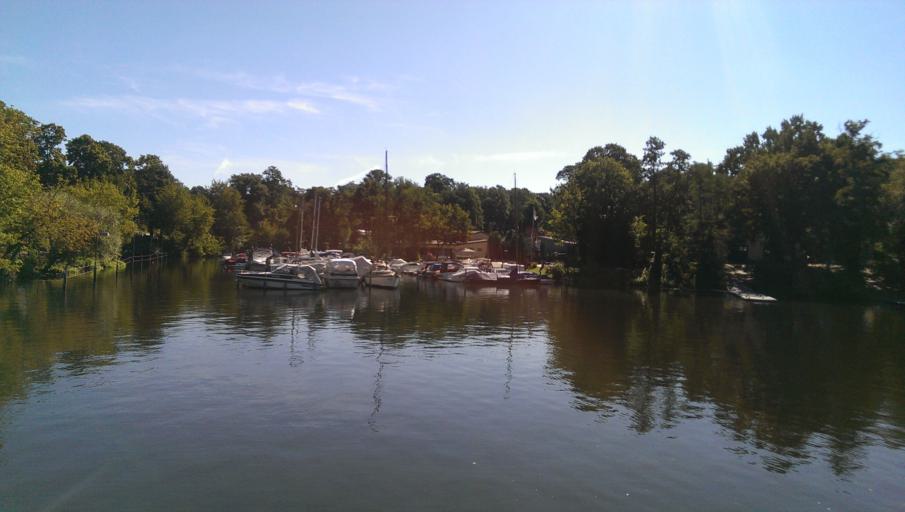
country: DE
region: Berlin
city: Wannsee
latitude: 52.4204
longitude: 13.1713
